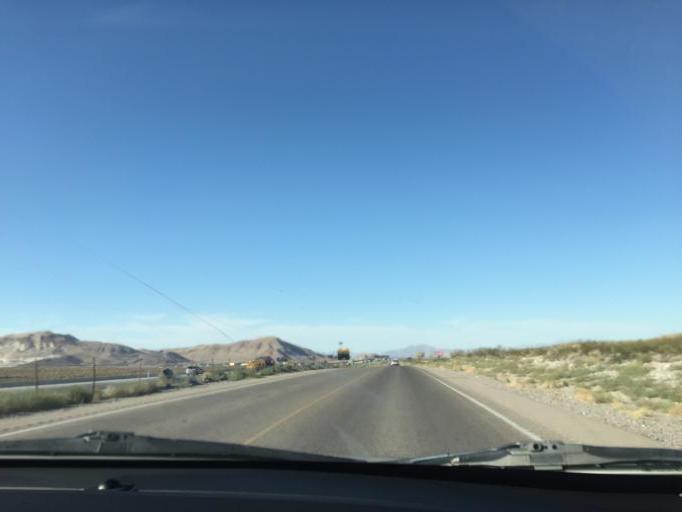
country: US
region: Nevada
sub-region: Clark County
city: Enterprise
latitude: 35.9081
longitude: -115.2082
